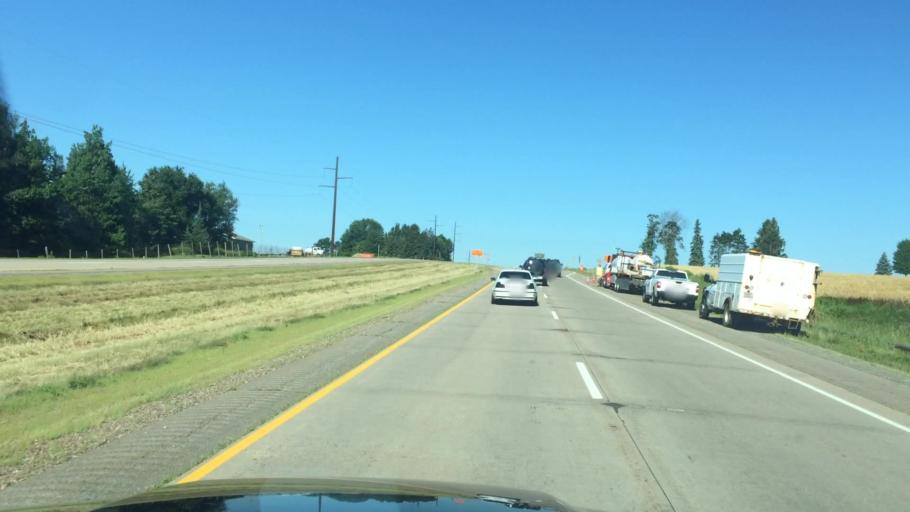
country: US
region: Wisconsin
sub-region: Marathon County
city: Edgar
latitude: 44.9446
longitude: -89.9229
